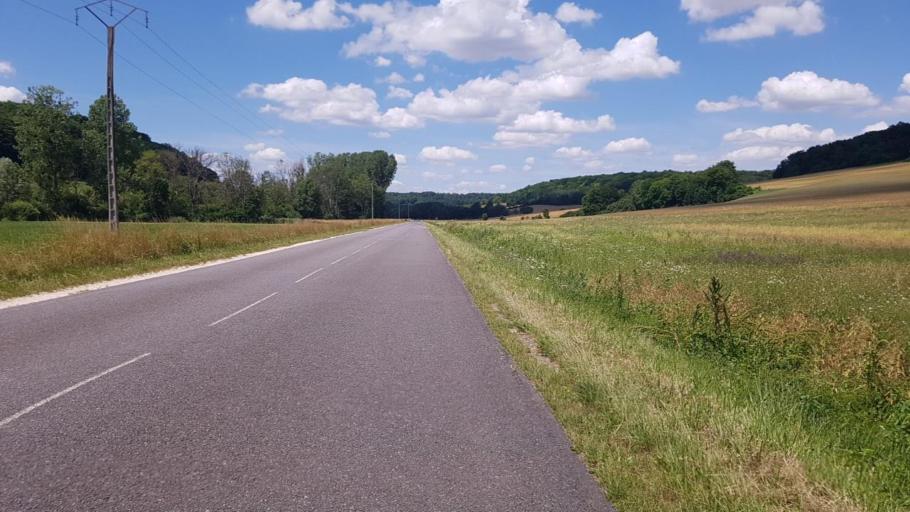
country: FR
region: Lorraine
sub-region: Departement de la Meuse
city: Ligny-en-Barrois
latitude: 48.6419
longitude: 5.4369
